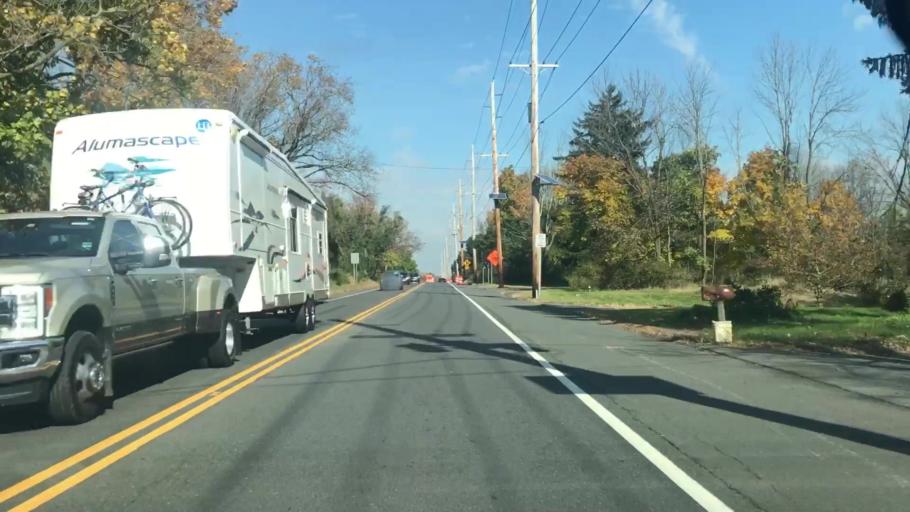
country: US
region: New Jersey
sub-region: Somerset County
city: Bloomingdale
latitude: 40.4504
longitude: -74.6615
